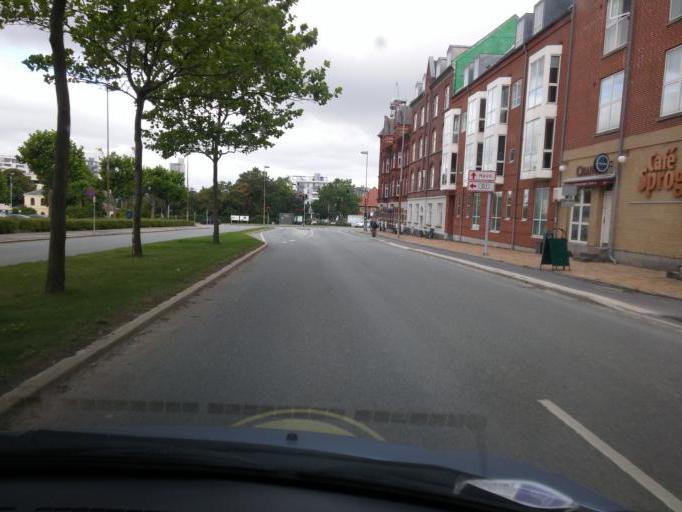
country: DK
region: South Denmark
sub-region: Odense Kommune
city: Odense
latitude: 55.4054
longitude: 10.3858
